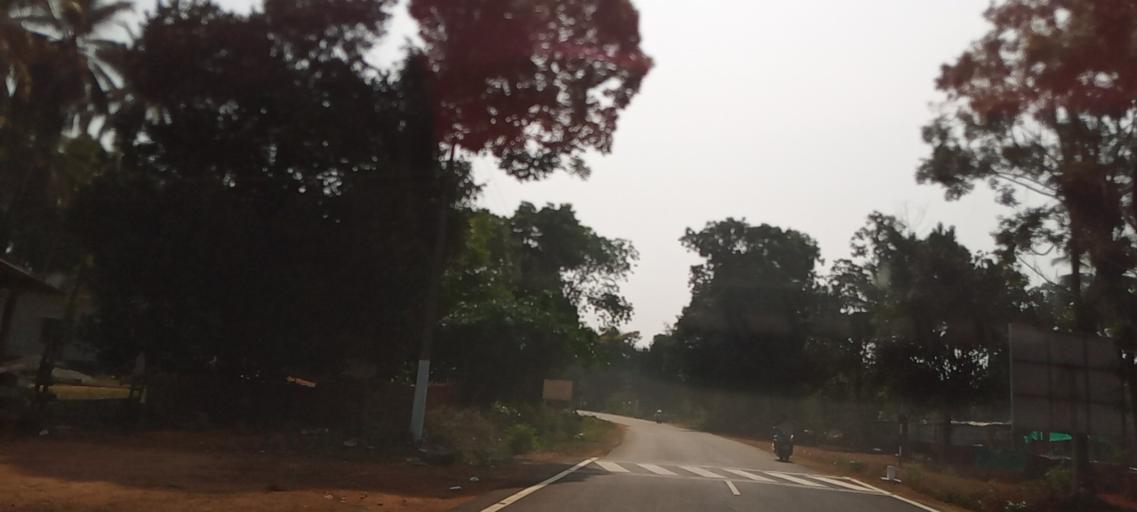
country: IN
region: Karnataka
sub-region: Udupi
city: Someshwar
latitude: 13.5177
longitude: 74.9351
